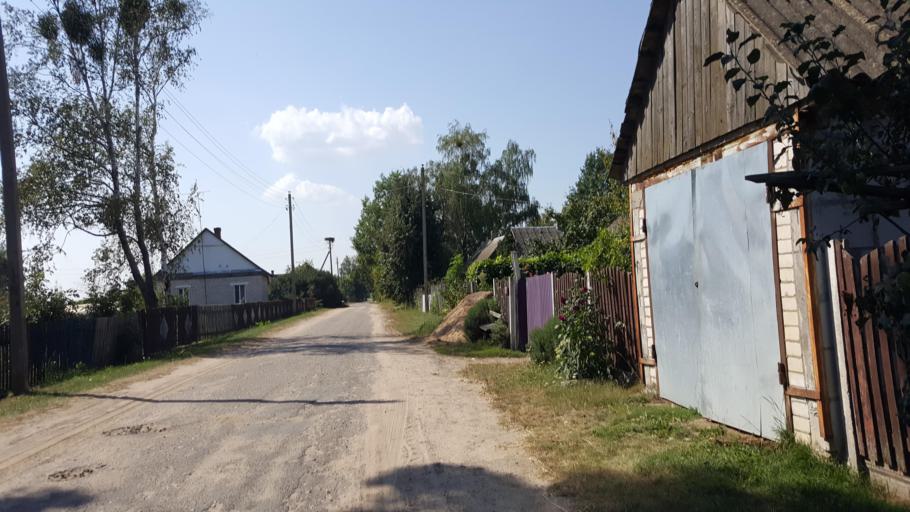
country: PL
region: Podlasie
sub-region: Powiat hajnowski
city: Czeremcha
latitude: 52.4790
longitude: 23.5380
